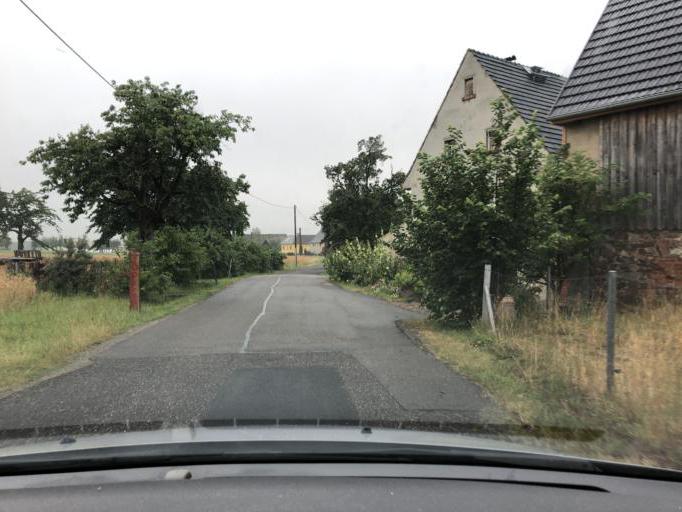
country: DE
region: Thuringia
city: Langenleuba-Niederhain
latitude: 50.9933
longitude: 12.6493
